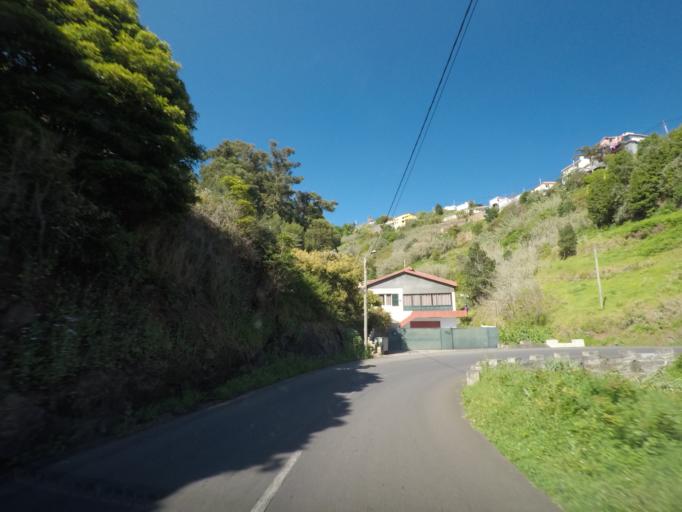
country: PT
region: Madeira
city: Ponta do Sol
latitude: 32.6978
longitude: -17.1027
